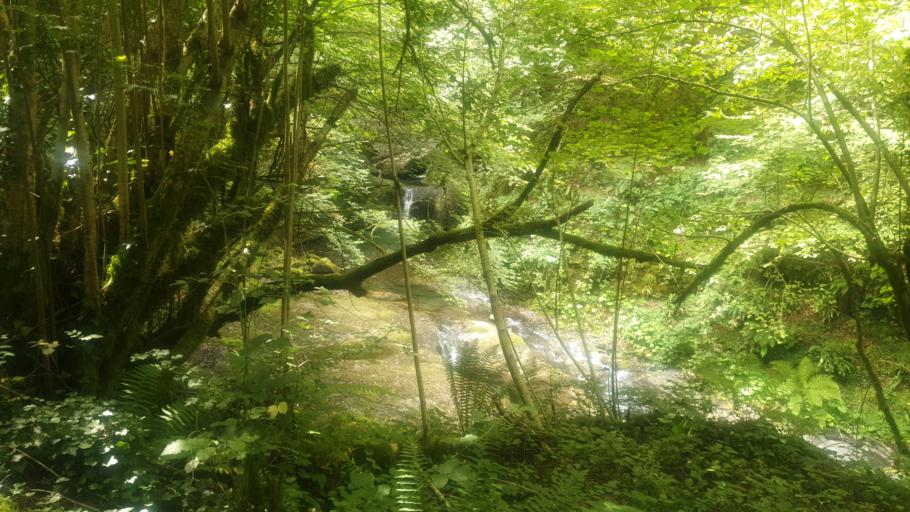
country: FR
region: Aquitaine
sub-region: Departement des Pyrenees-Atlantiques
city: Ogeu-les-Bains
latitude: 43.0313
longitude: -0.5542
